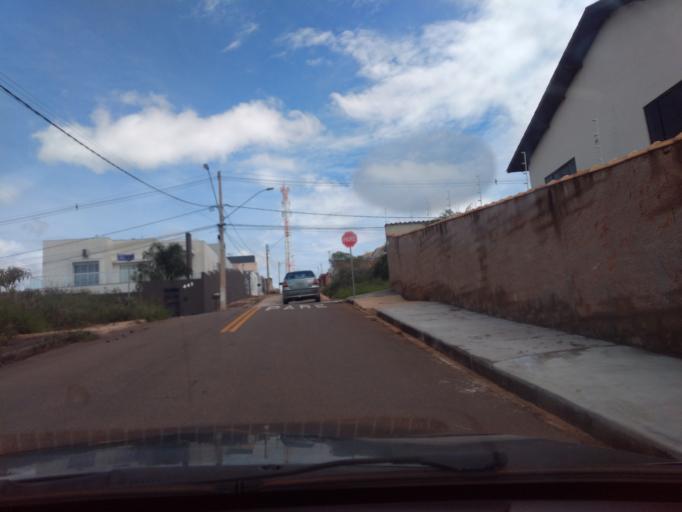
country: BR
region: Minas Gerais
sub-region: Tres Coracoes
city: Tres Coracoes
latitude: -21.6693
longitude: -45.2780
